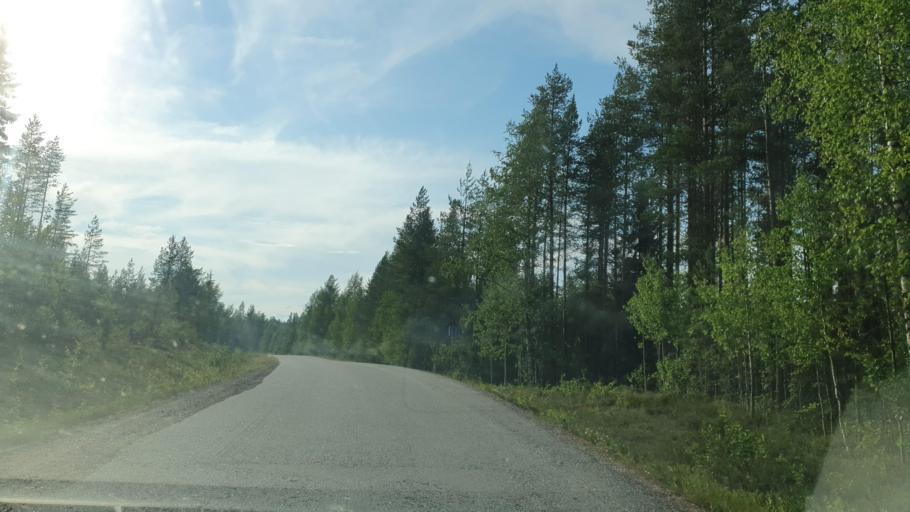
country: FI
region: Kainuu
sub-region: Kehys-Kainuu
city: Kuhmo
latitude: 64.2791
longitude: 29.4260
